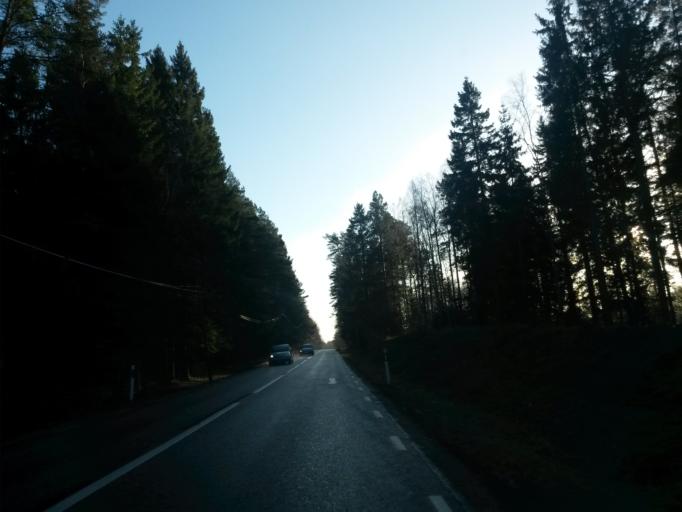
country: SE
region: Vaestra Goetaland
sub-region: Vargarda Kommun
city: Vargarda
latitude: 57.9359
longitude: 12.8522
